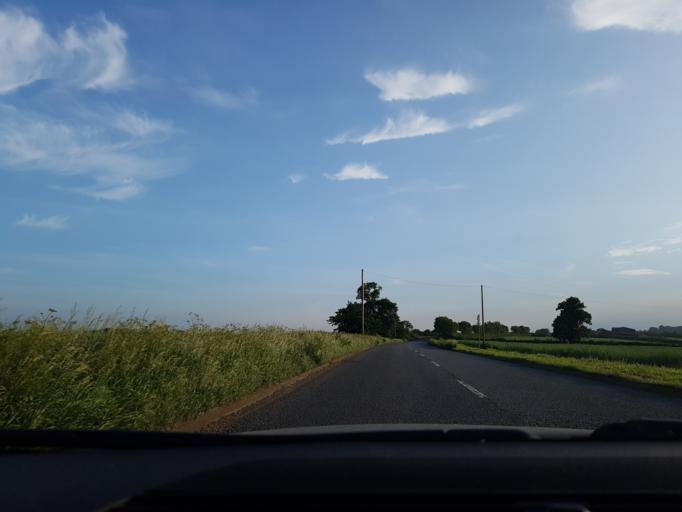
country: GB
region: England
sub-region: Buckinghamshire
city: Buckingham
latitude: 52.0092
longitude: -0.9506
